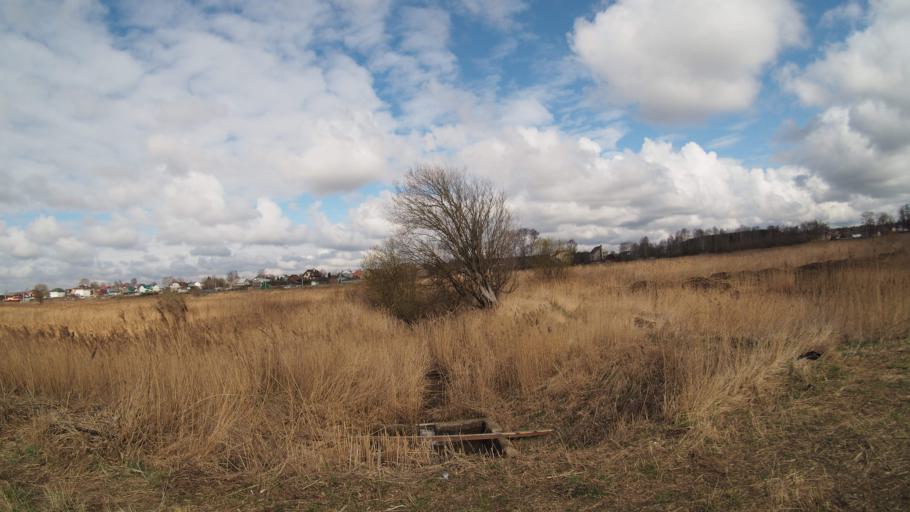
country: RU
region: Moskovskaya
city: Malyshevo
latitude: 55.5522
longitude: 38.3144
